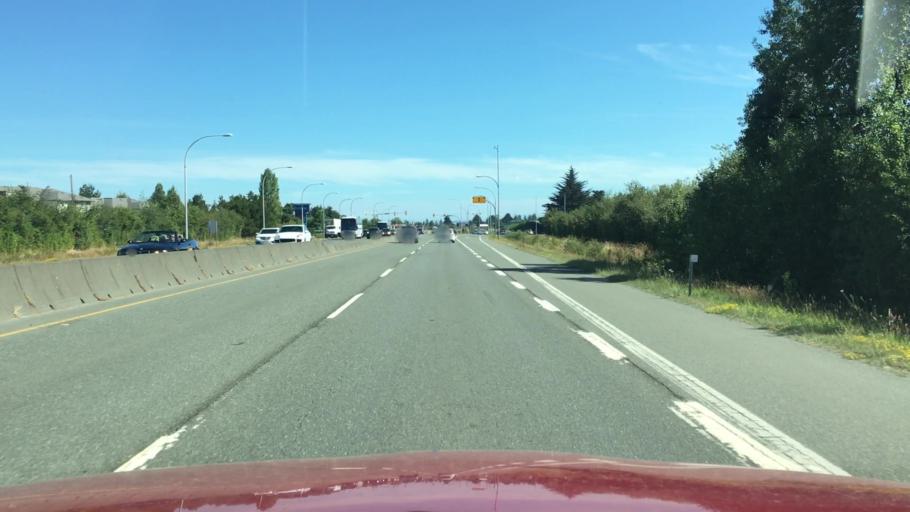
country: CA
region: British Columbia
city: North Saanich
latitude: 48.6514
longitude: -123.4090
